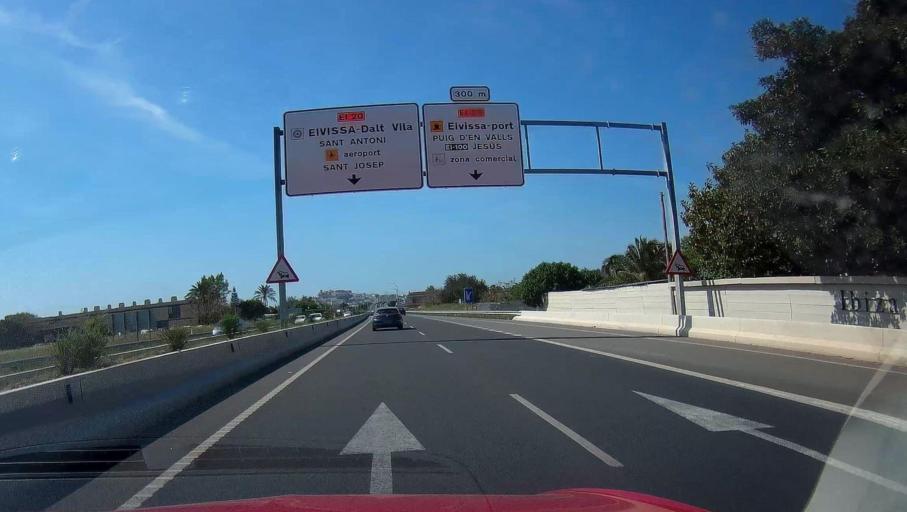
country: ES
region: Balearic Islands
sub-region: Illes Balears
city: Ibiza
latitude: 38.9313
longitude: 1.4432
